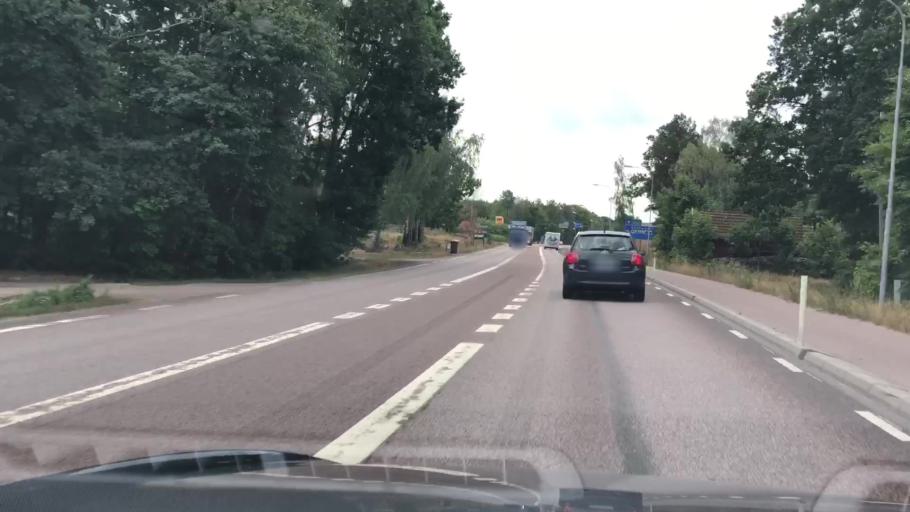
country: SE
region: Blekinge
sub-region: Karlskrona Kommun
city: Jaemjoe
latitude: 56.2627
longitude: 15.9503
